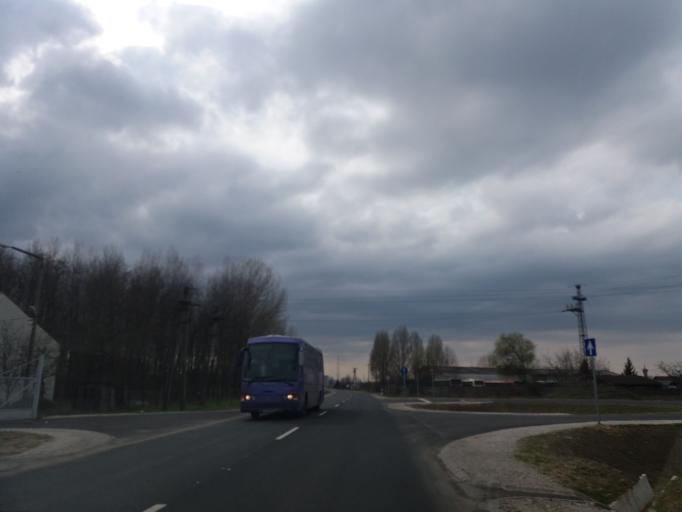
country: HU
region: Szabolcs-Szatmar-Bereg
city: Kisvarda
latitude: 48.2012
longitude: 22.0895
